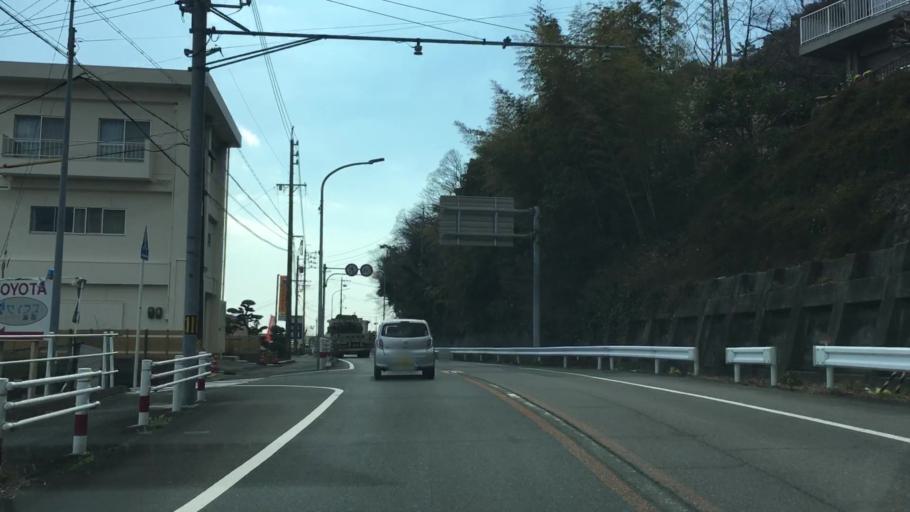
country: JP
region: Aichi
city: Gamagori
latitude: 34.8097
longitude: 137.2661
